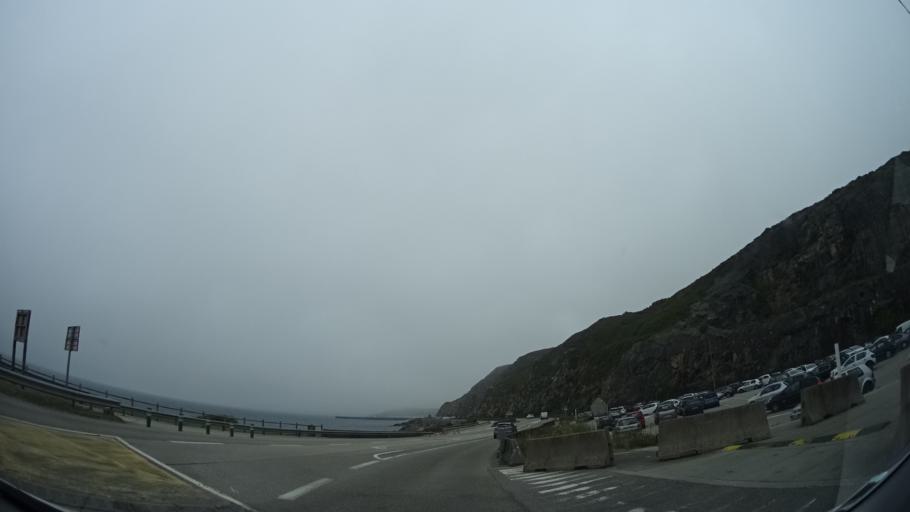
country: FR
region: Lower Normandy
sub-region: Departement de la Manche
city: Flamanville
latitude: 49.5449
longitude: -1.8738
